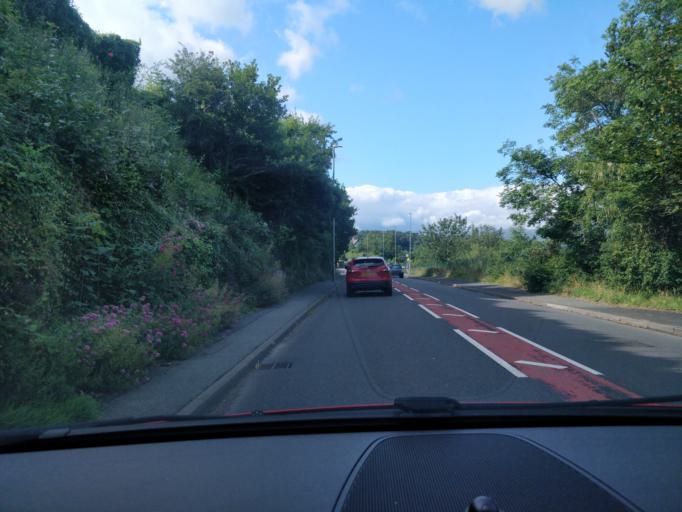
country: GB
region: Wales
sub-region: Conwy
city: Llansantffraid Glan Conwy
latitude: 53.2659
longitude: -3.7984
